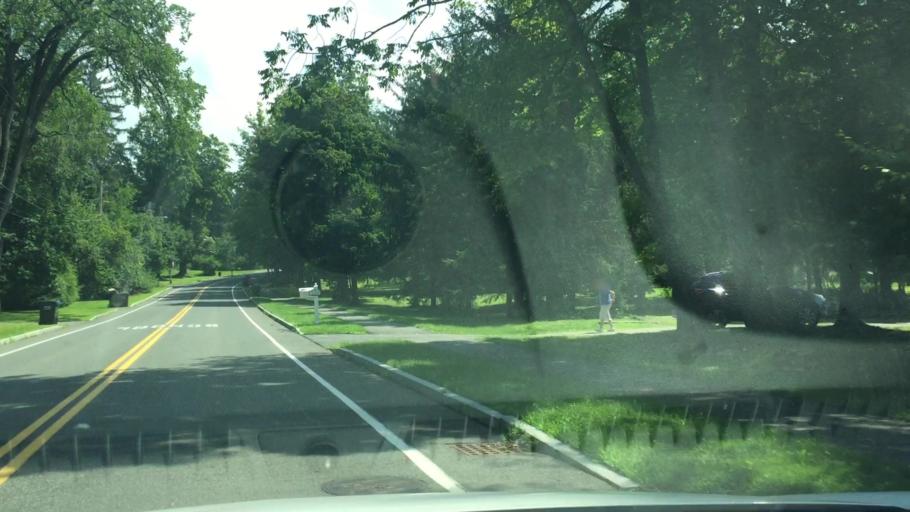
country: US
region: Massachusetts
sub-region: Berkshire County
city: Lenox
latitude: 42.3569
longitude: -73.2954
